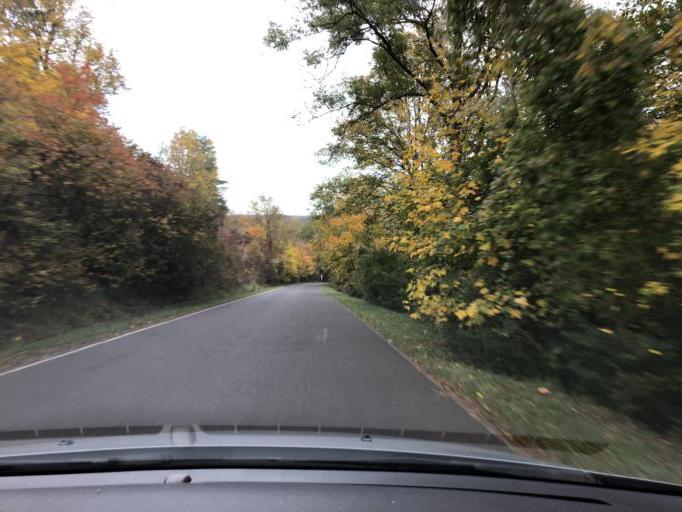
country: DE
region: Thuringia
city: Hetschburg
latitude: 50.9150
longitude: 11.2938
